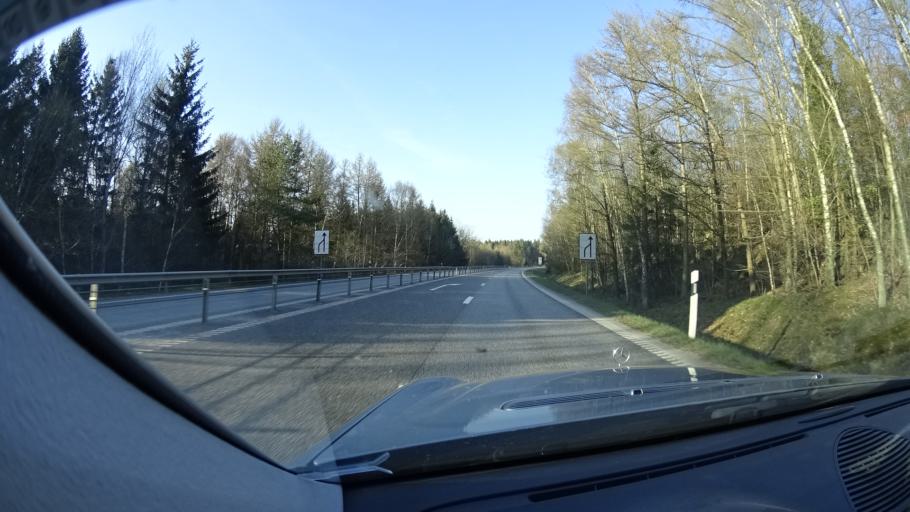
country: SE
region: Skane
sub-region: Hoors Kommun
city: Satofta
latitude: 55.9128
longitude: 13.5247
